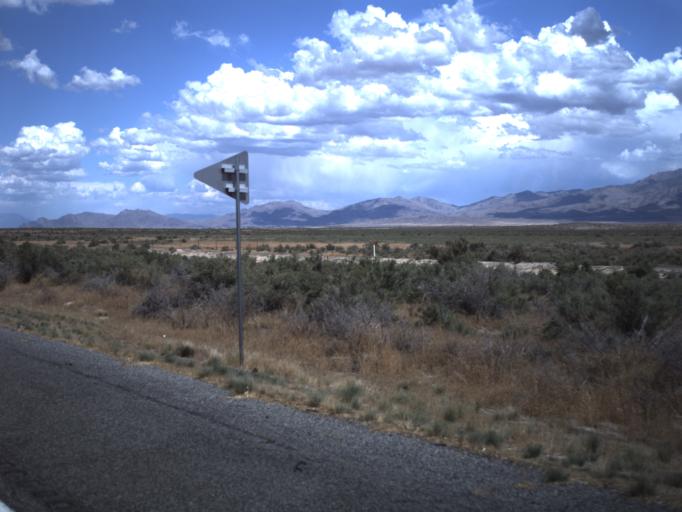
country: US
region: Utah
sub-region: Millard County
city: Delta
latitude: 39.4221
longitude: -112.4754
